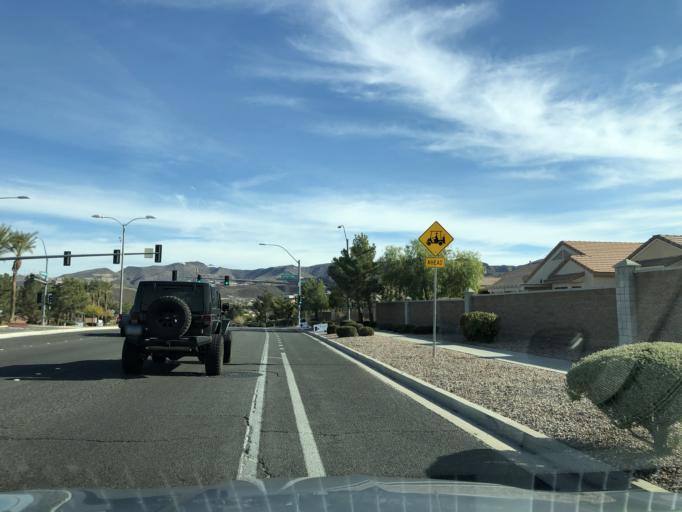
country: US
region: Nevada
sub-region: Clark County
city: Whitney
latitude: 36.0050
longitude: -115.0777
